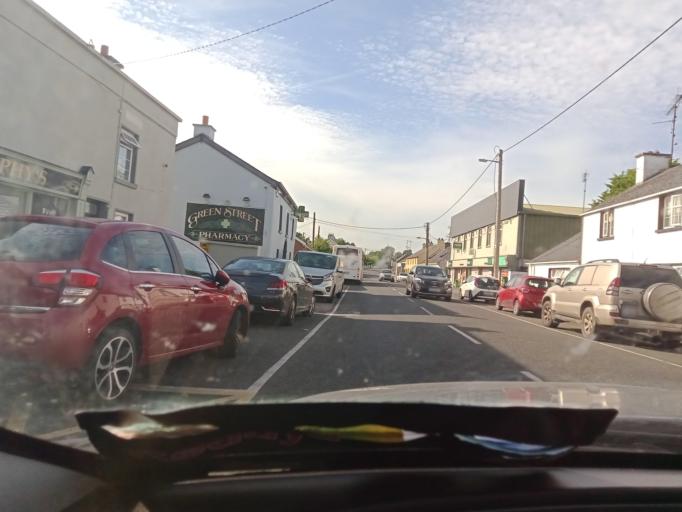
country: IE
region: Leinster
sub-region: An Iarmhi
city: Castlepollard
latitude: 53.6800
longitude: -7.2992
